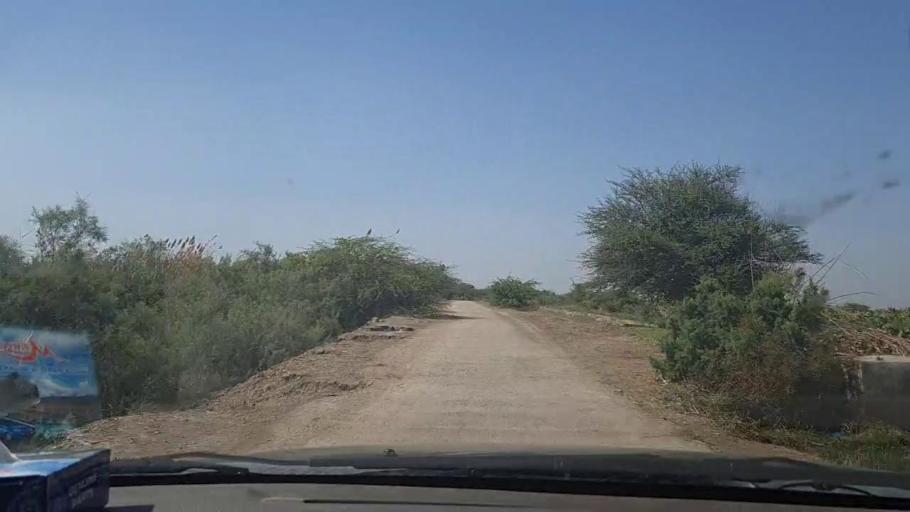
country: PK
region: Sindh
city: Chuhar Jamali
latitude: 24.2844
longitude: 67.7599
